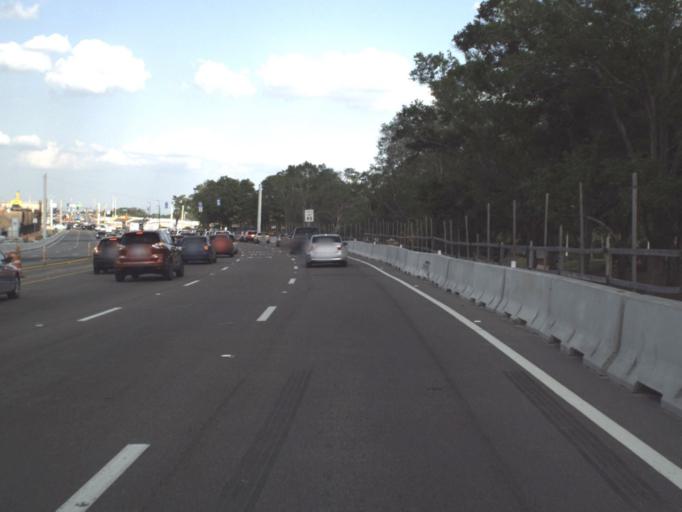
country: US
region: Florida
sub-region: Orange County
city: Eatonville
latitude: 28.6308
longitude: -81.3964
